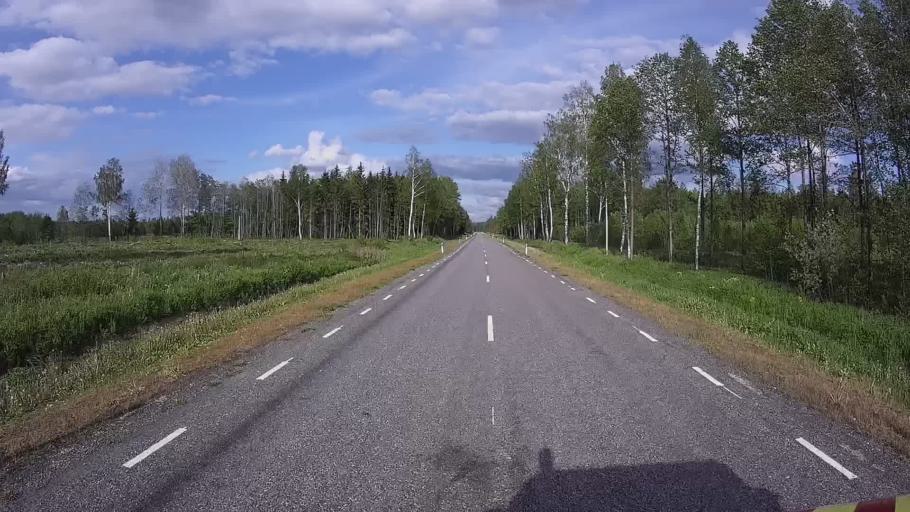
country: EE
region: Jogevamaa
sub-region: Mustvee linn
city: Mustvee
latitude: 59.0220
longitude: 27.0505
